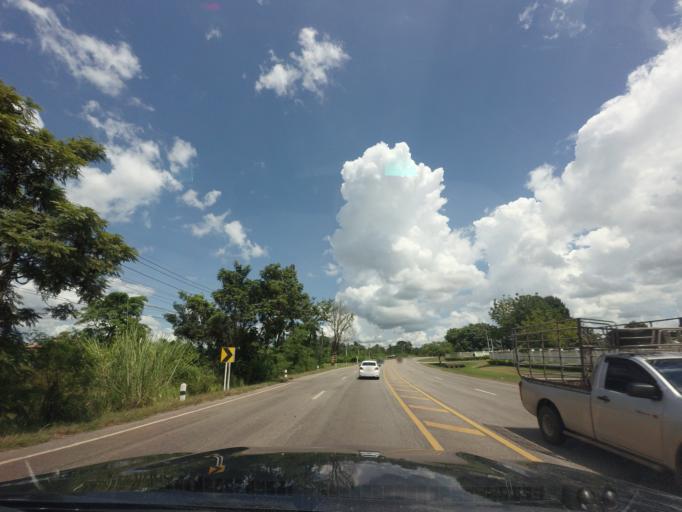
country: TH
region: Changwat Udon Thani
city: Ban Dung
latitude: 17.6864
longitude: 103.1993
